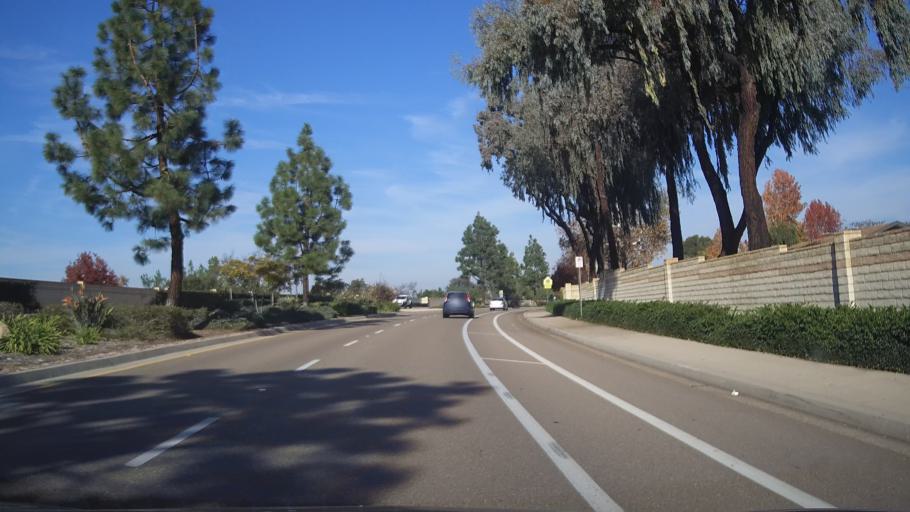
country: US
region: California
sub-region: San Diego County
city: La Mesa
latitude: 32.8139
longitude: -117.1059
